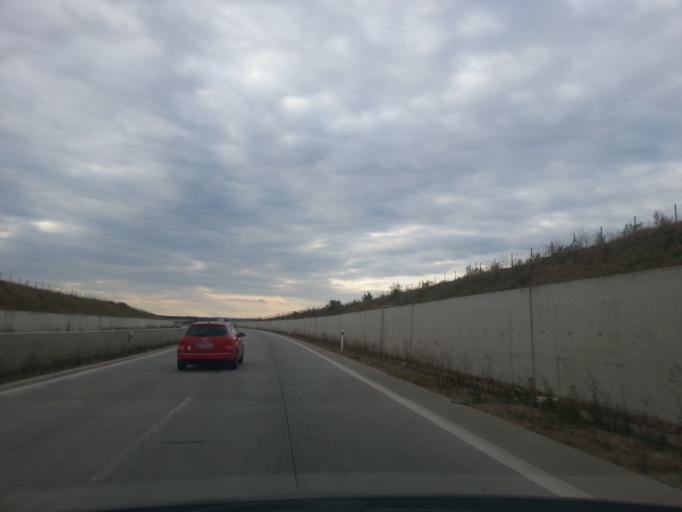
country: CZ
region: Central Bohemia
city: Hostivice
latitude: 50.0928
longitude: 14.2487
